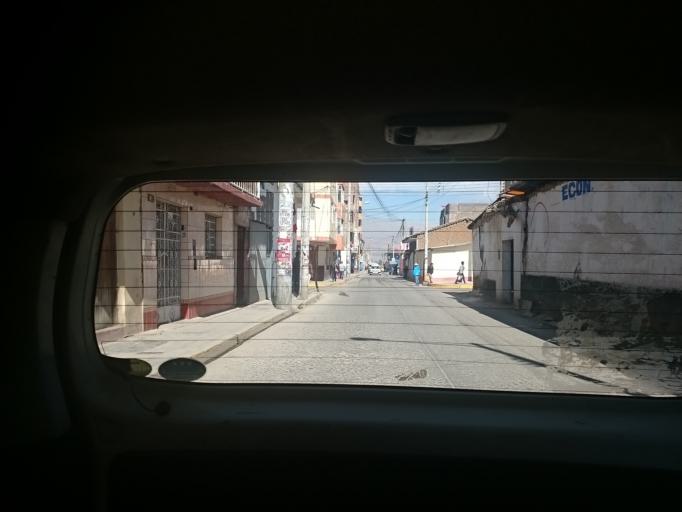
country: PE
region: Junin
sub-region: Provincia de Huancayo
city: El Tambo
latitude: -12.0738
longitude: -75.2102
